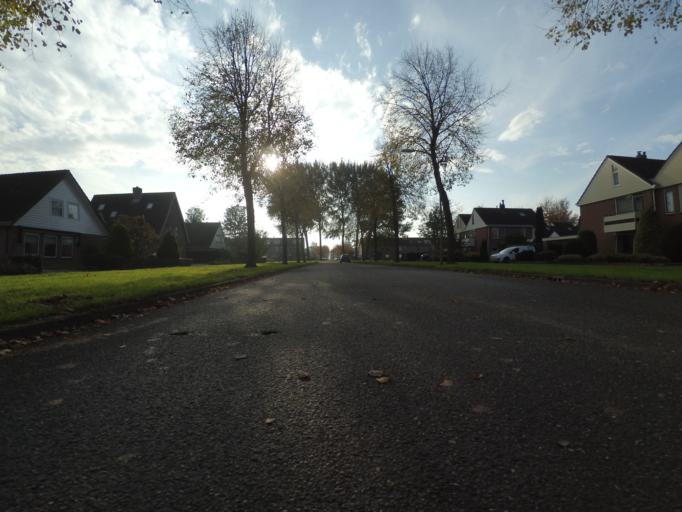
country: NL
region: Flevoland
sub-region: Gemeente Zeewolde
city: Zeewolde
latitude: 52.3366
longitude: 5.5376
